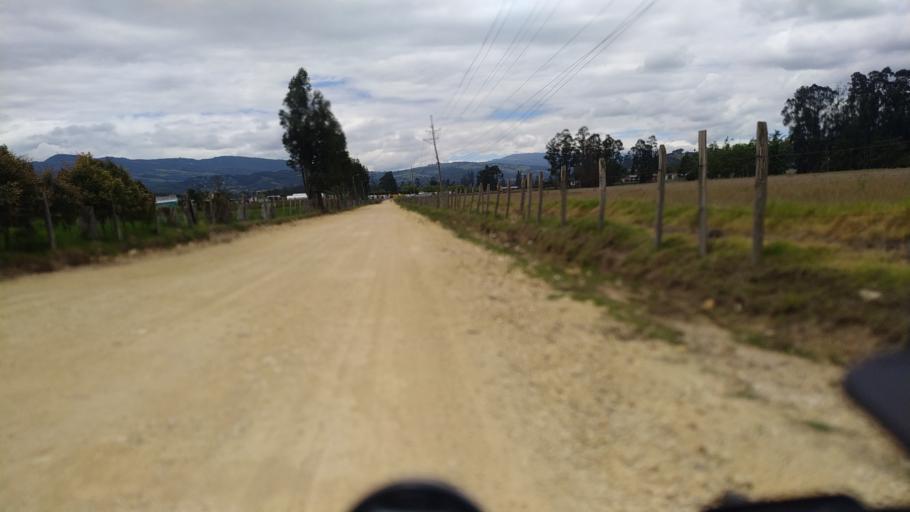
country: CO
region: Boyaca
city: Duitama
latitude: 5.7933
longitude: -73.0699
